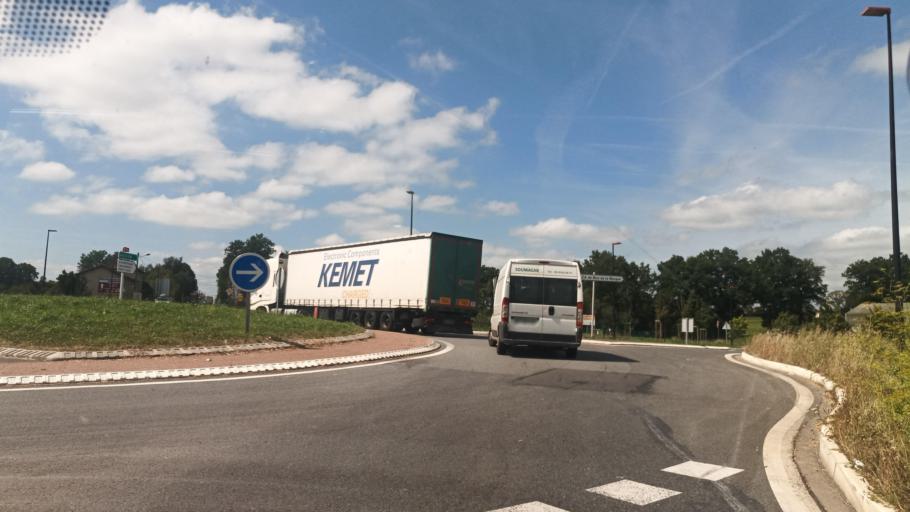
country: FR
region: Poitou-Charentes
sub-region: Departement de la Charente
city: Loubert
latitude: 45.8847
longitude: 0.5924
